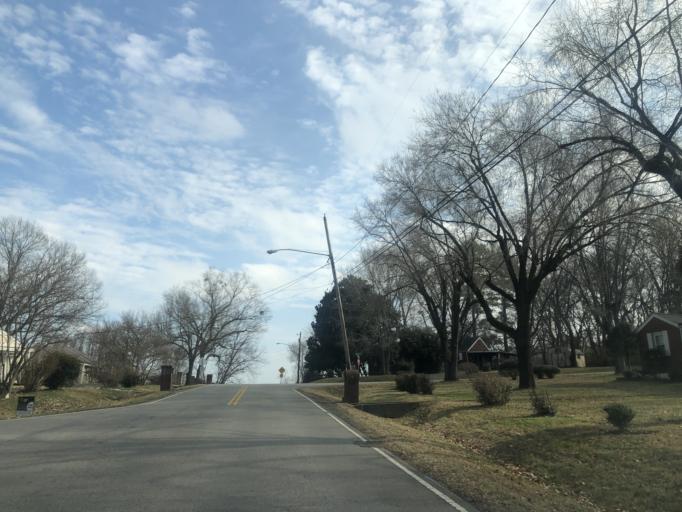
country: US
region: Tennessee
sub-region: Davidson County
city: Oak Hill
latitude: 36.1133
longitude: -86.7165
